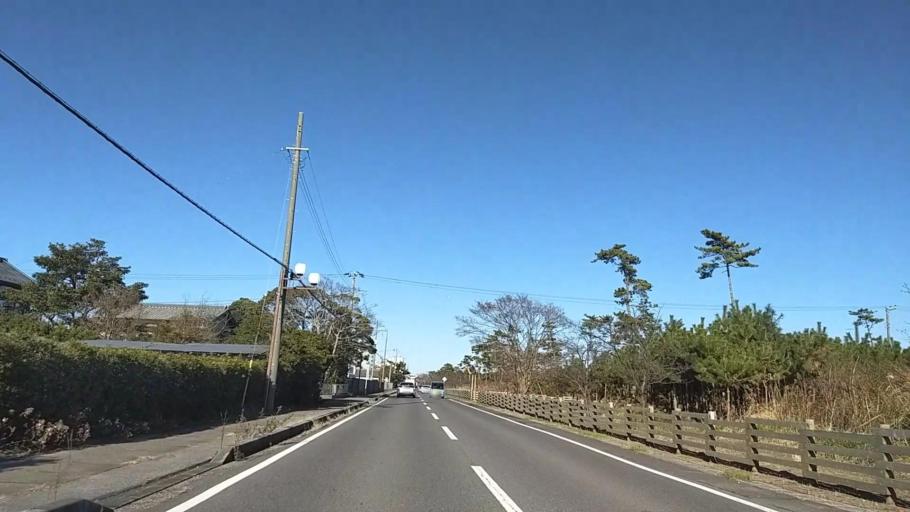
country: JP
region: Chiba
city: Mobara
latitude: 35.4237
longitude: 140.3940
